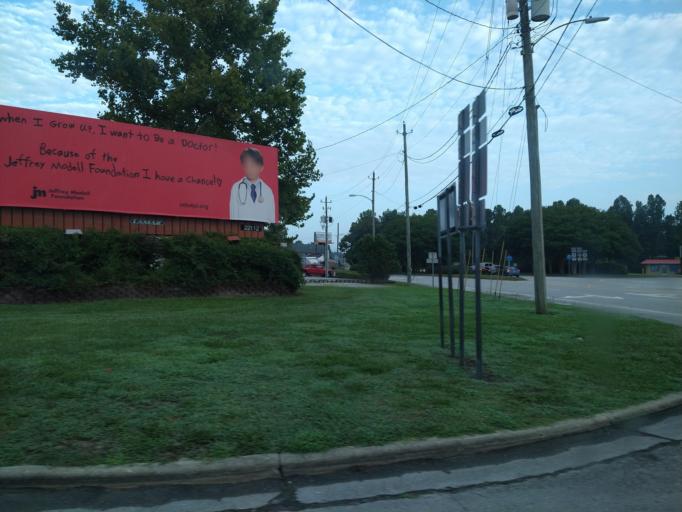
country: US
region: North Carolina
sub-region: Onslow County
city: Jacksonville
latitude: 34.7541
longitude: -77.4249
